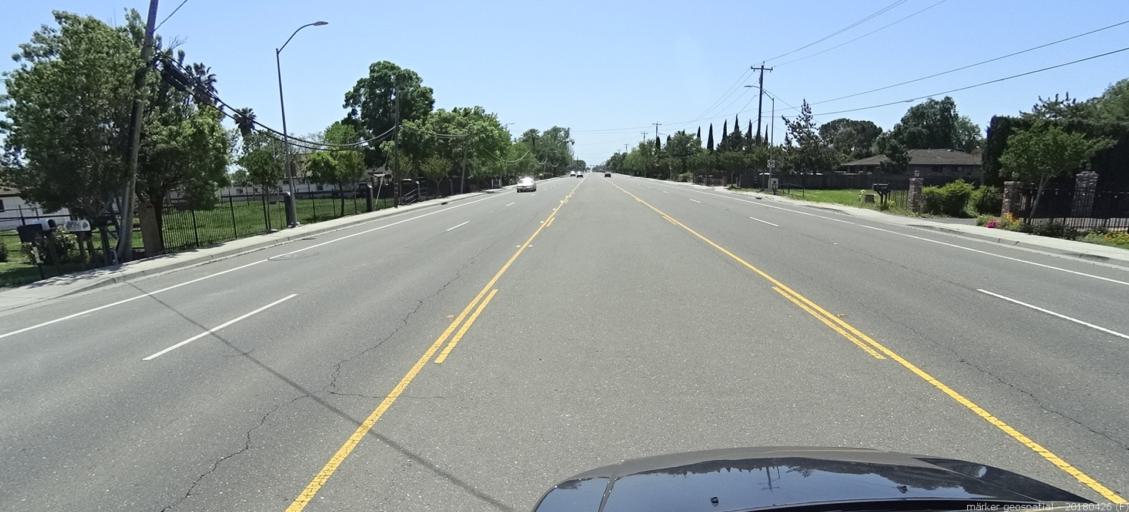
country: US
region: California
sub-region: Yolo County
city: West Sacramento
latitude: 38.5439
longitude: -121.5455
